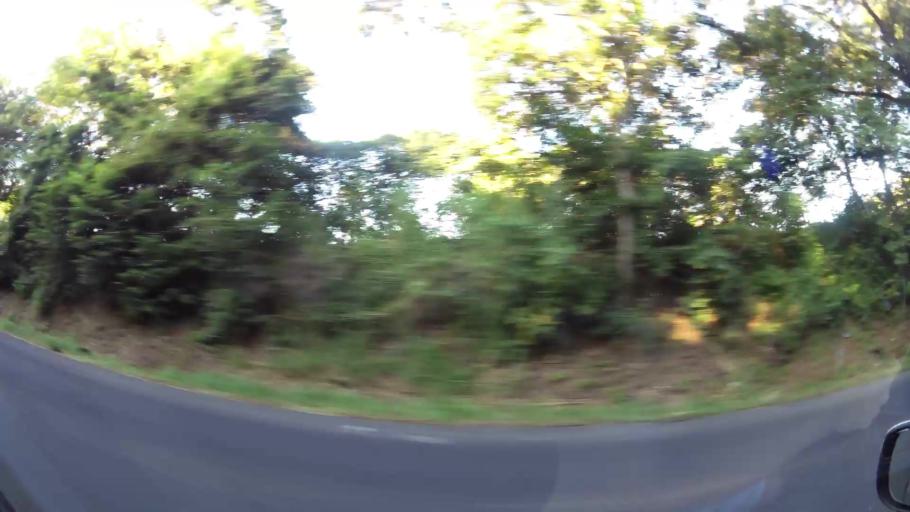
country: CR
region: Puntarenas
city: Esparza
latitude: 10.0029
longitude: -84.7204
